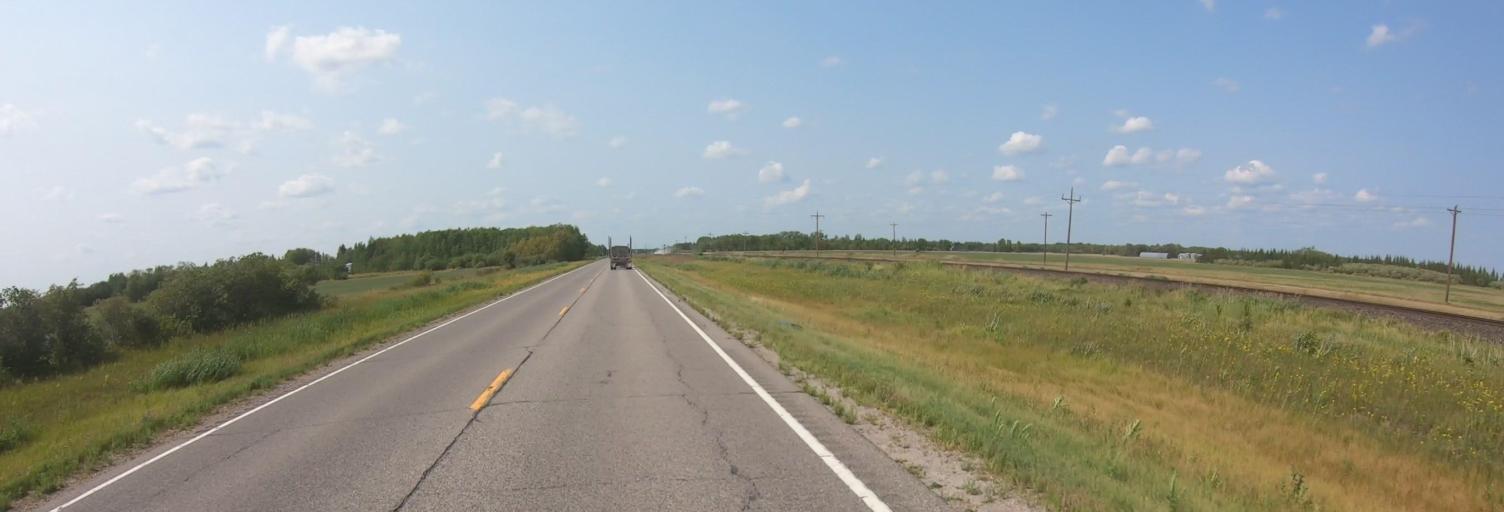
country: US
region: Minnesota
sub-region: Roseau County
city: Warroad
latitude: 48.8681
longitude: -95.2577
